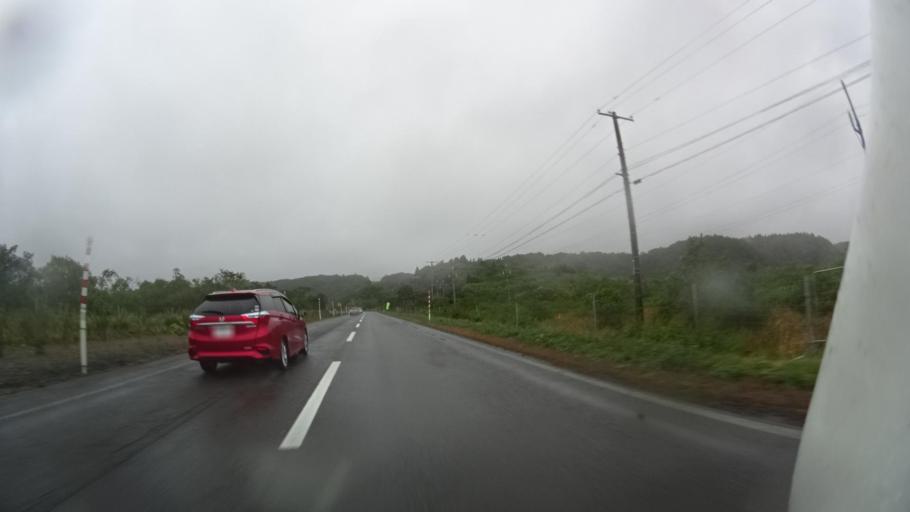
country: JP
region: Hokkaido
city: Kushiro
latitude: 43.1056
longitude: 144.8780
